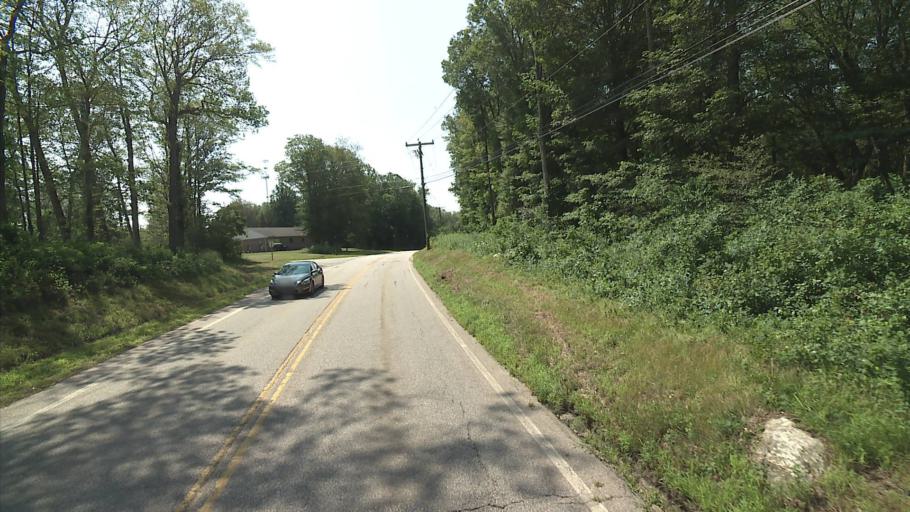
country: US
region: Connecticut
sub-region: New London County
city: Montville Center
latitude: 41.4240
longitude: -72.2143
